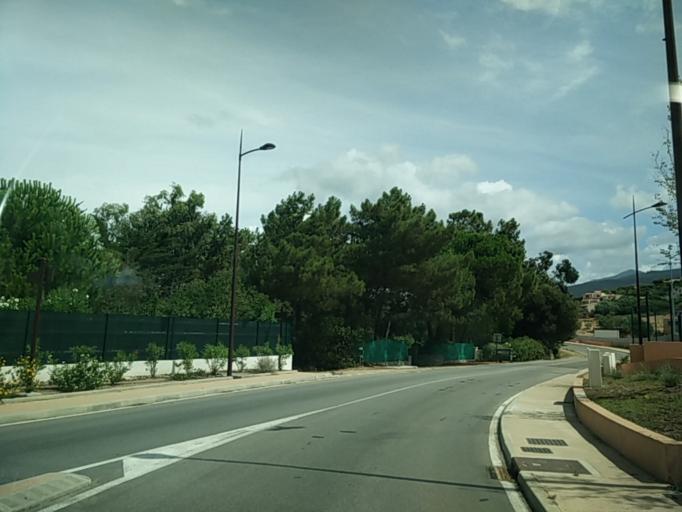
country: FR
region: Corsica
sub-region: Departement de la Corse-du-Sud
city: Pietrosella
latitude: 41.8261
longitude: 8.7803
